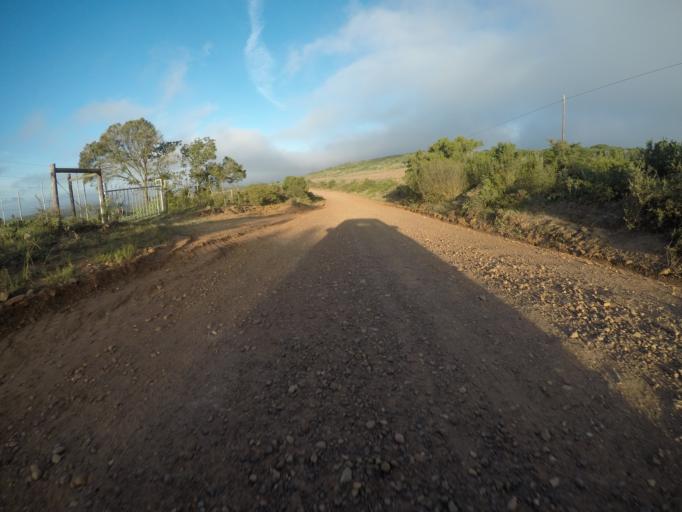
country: ZA
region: Western Cape
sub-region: Eden District Municipality
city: Mossel Bay
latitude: -34.1448
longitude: 22.0173
